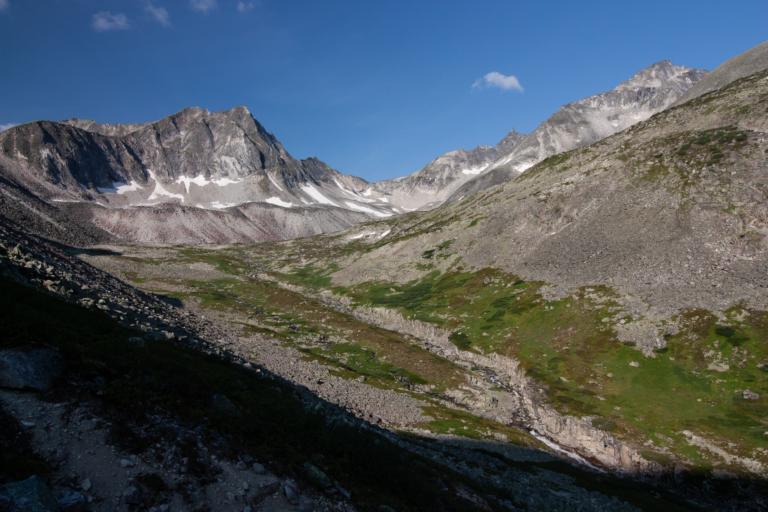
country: RU
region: Respublika Buryatiya
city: Novyy Uoyan
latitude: 56.2235
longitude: 110.9445
